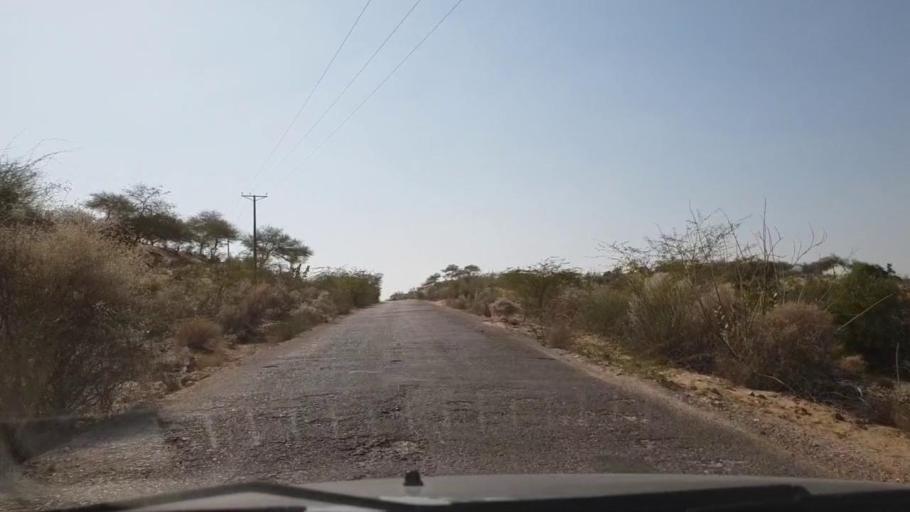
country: PK
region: Sindh
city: Diplo
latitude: 24.5431
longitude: 69.6471
